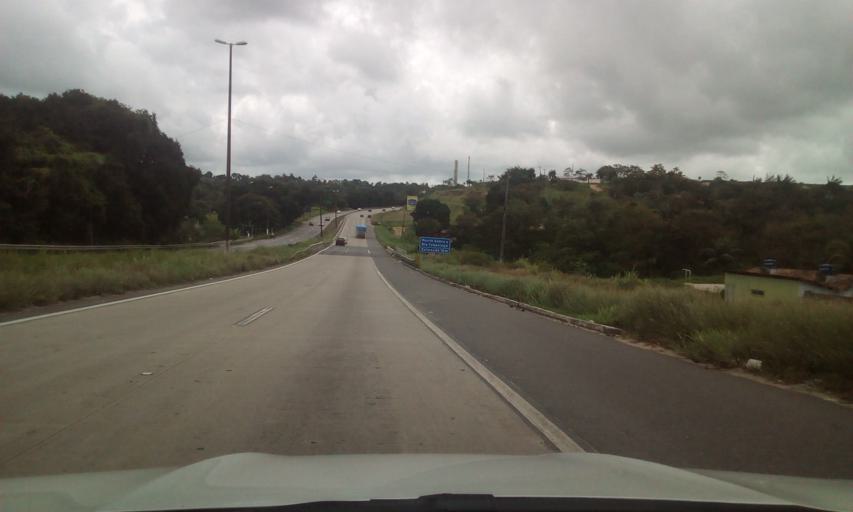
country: BR
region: Pernambuco
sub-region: Igarassu
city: Igarassu
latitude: -7.8087
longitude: -34.9221
